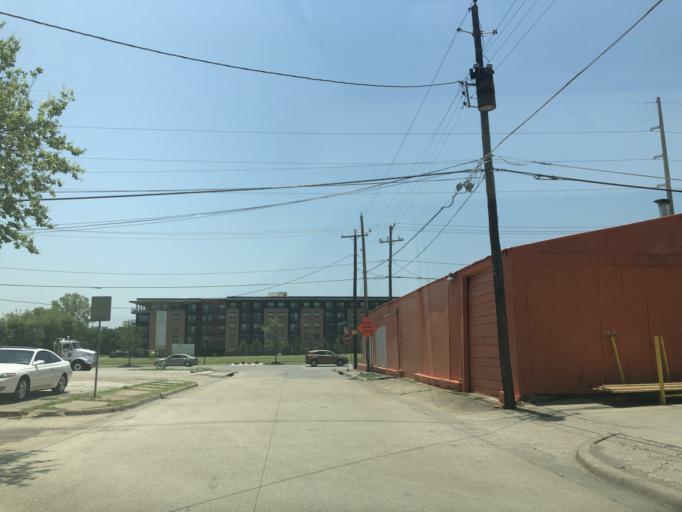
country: US
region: Texas
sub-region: Dallas County
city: Dallas
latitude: 32.7792
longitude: -96.8379
